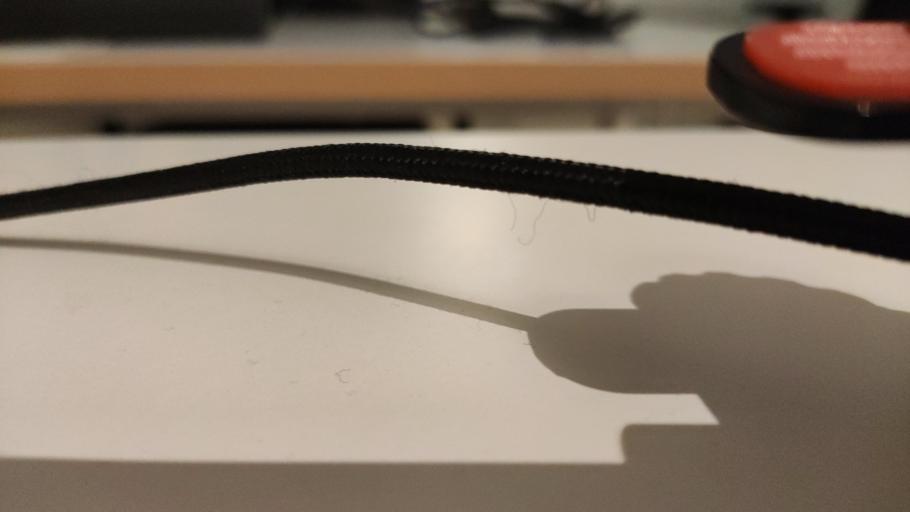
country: RU
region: Moskovskaya
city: Dmitrov
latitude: 56.3577
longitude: 37.5263
